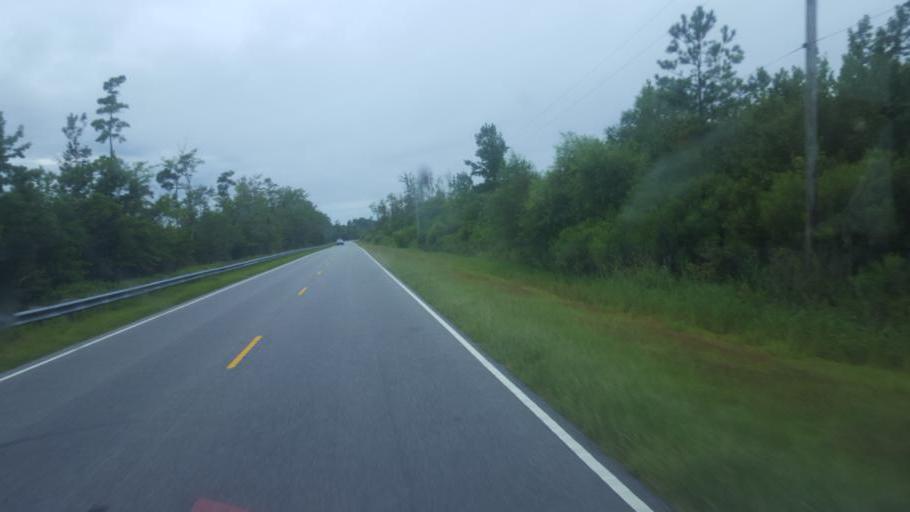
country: US
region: North Carolina
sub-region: Tyrrell County
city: Columbia
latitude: 35.9070
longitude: -76.1024
